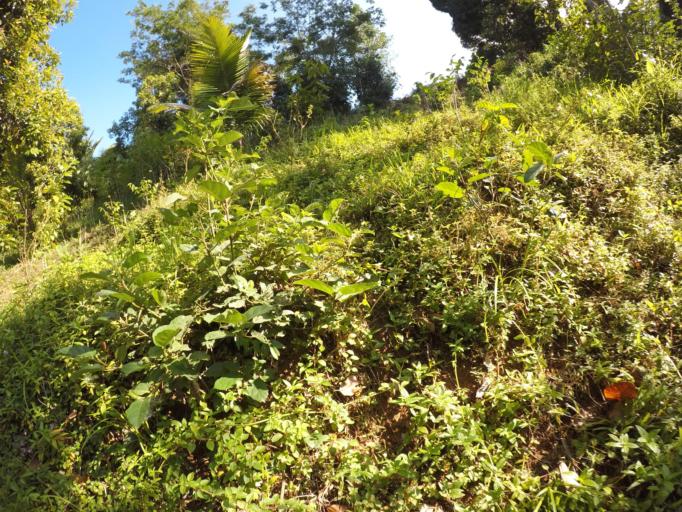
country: TZ
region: Pemba South
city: Mtambile
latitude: -5.3868
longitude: 39.7270
